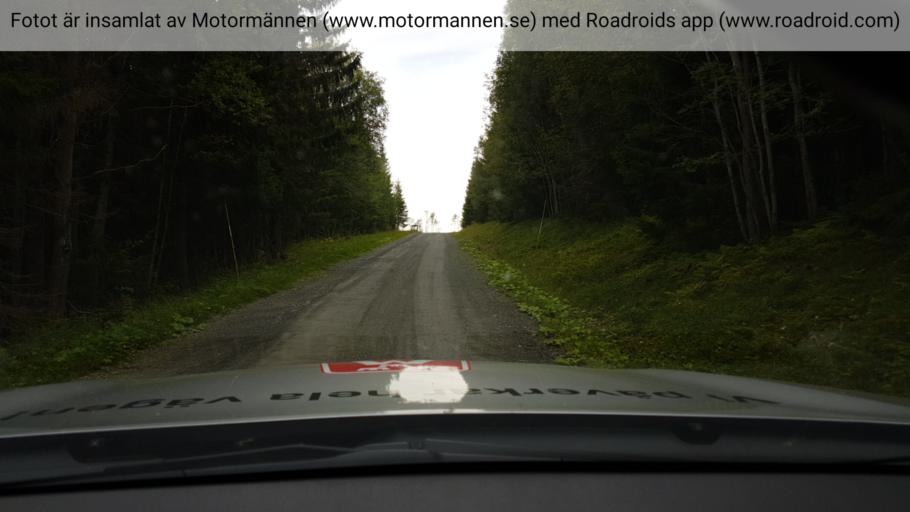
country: SE
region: Jaemtland
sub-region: Krokoms Kommun
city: Valla
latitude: 63.5908
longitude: 14.0019
